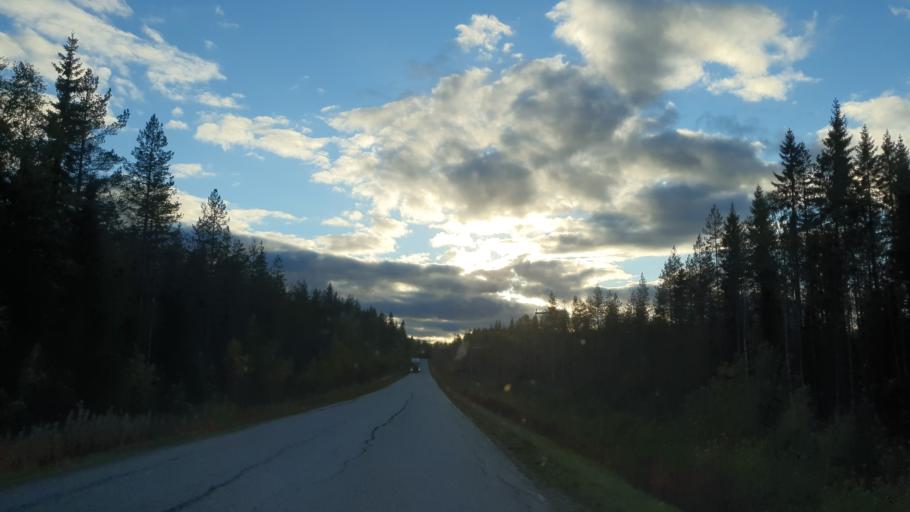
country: FI
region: Kainuu
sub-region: Kehys-Kainuu
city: Kuhmo
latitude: 63.9488
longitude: 29.7806
